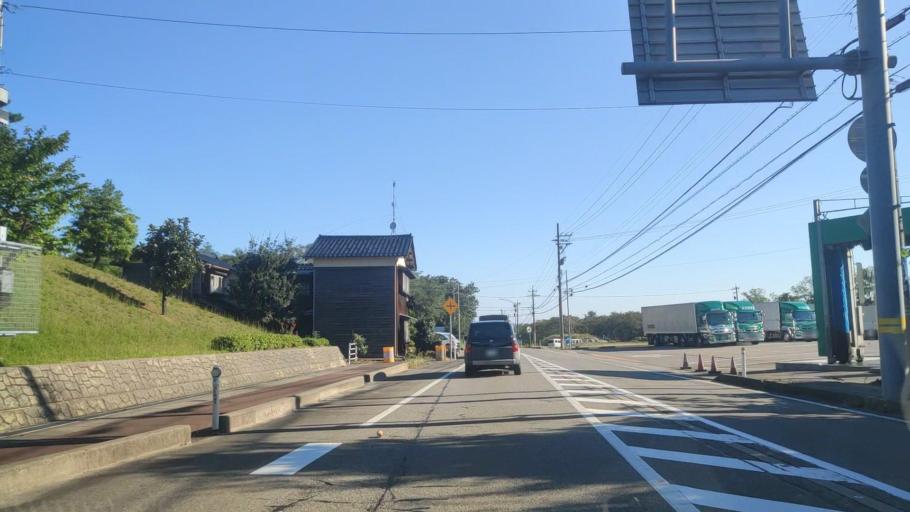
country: JP
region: Ishikawa
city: Tsubata
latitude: 36.7799
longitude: 136.7354
